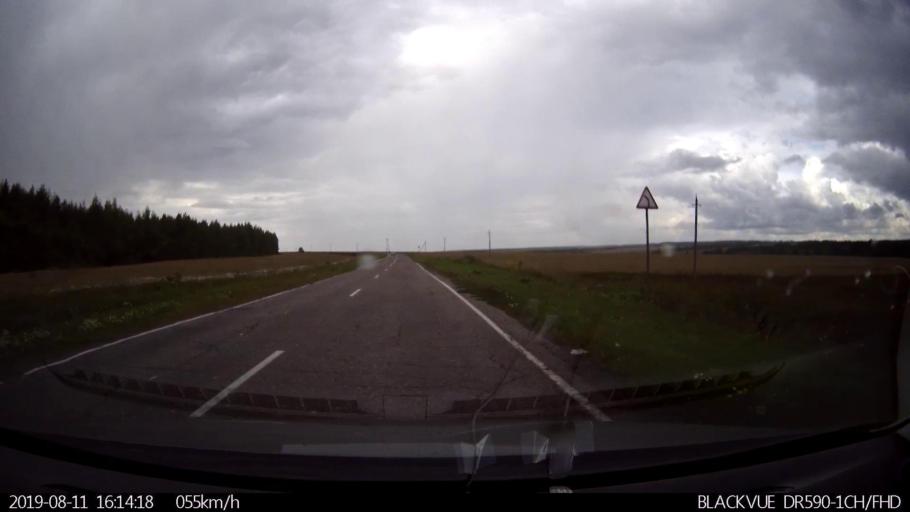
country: RU
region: Ulyanovsk
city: Ignatovka
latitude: 54.0269
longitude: 47.6344
